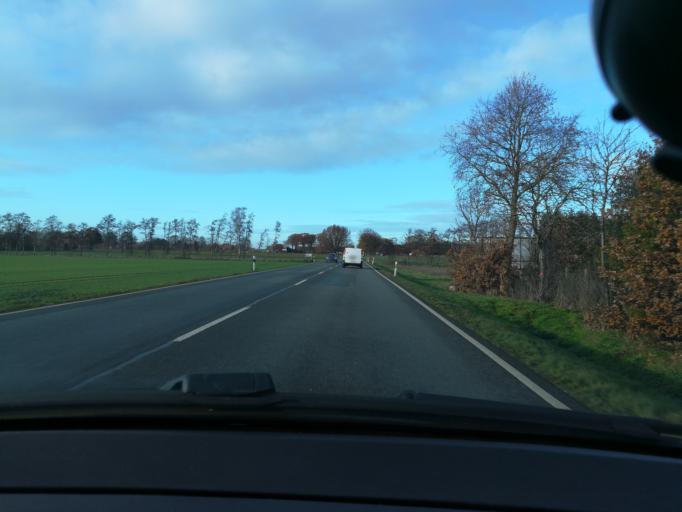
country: DE
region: Lower Saxony
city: Uchte
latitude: 52.5213
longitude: 8.8934
